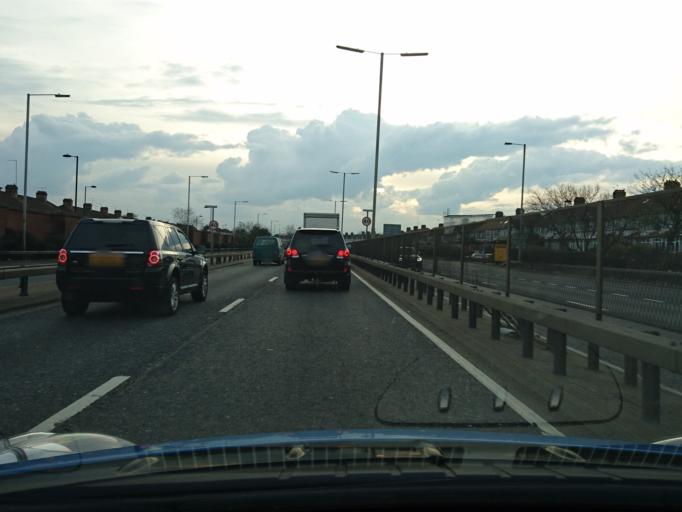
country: GB
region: England
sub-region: Greater London
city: Wood Green
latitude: 51.6163
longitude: -0.0916
